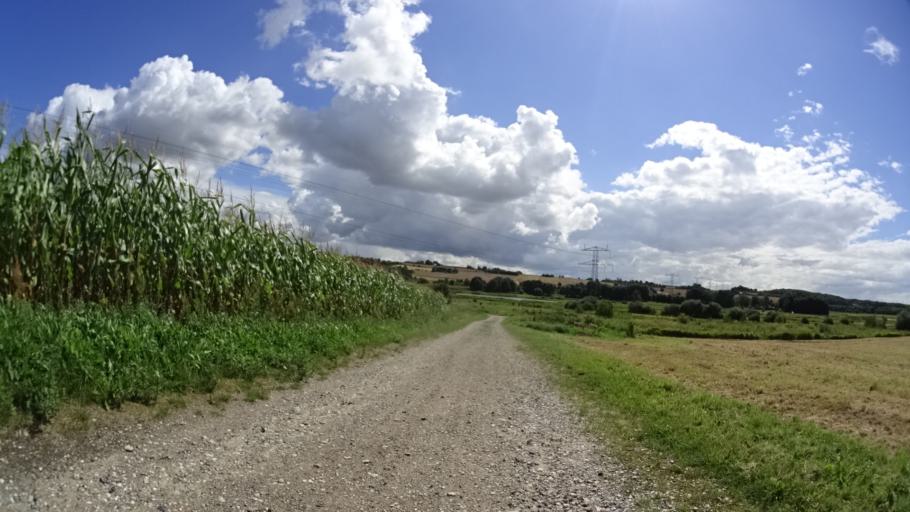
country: DK
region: Central Jutland
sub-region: Arhus Kommune
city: Framlev
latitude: 56.1357
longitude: 10.0433
